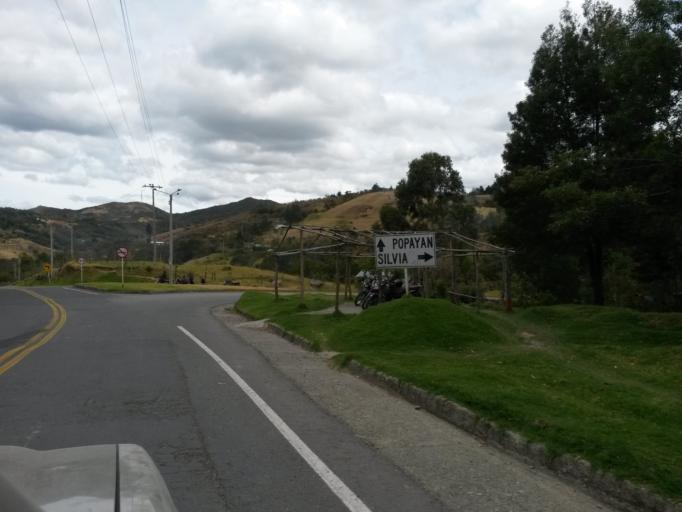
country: CO
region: Cauca
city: Totoro
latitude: 2.5109
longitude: -76.4064
